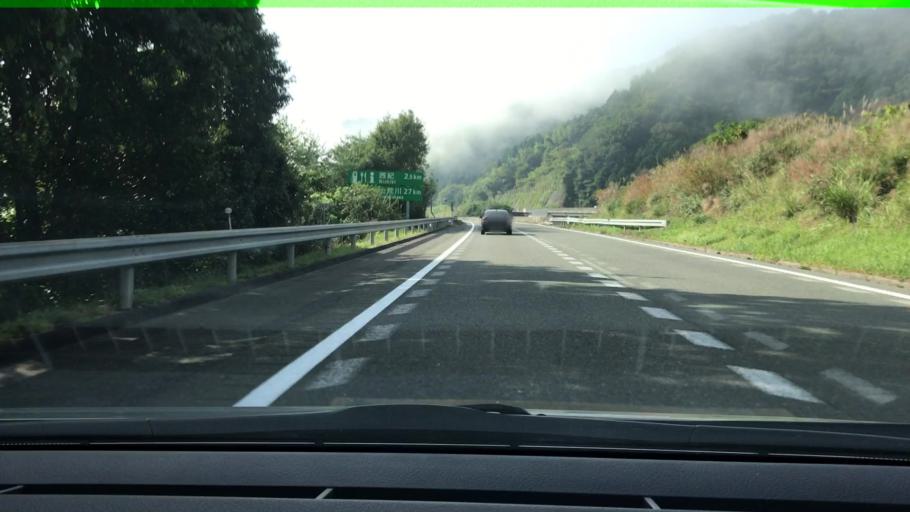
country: JP
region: Hyogo
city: Sasayama
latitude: 35.1140
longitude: 135.1657
